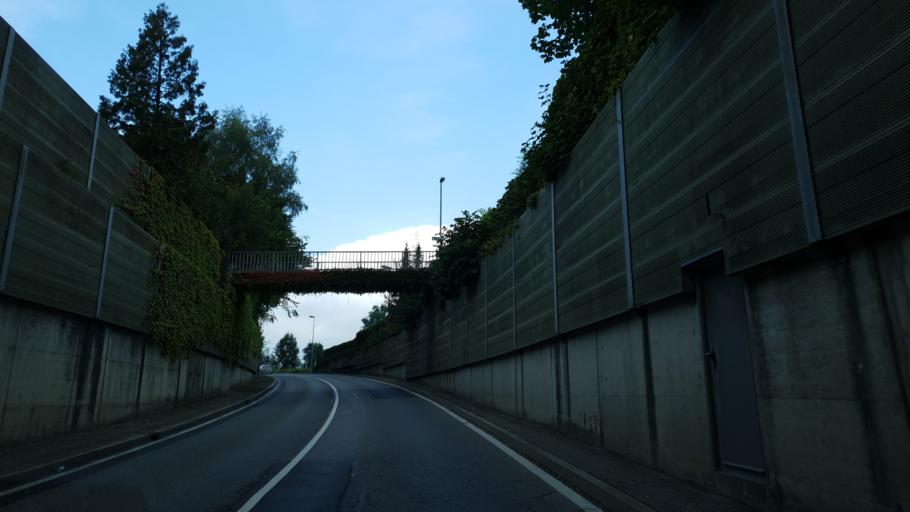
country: AT
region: Vorarlberg
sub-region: Politischer Bezirk Dornbirn
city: Dornbirn
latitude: 47.3972
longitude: 9.7247
